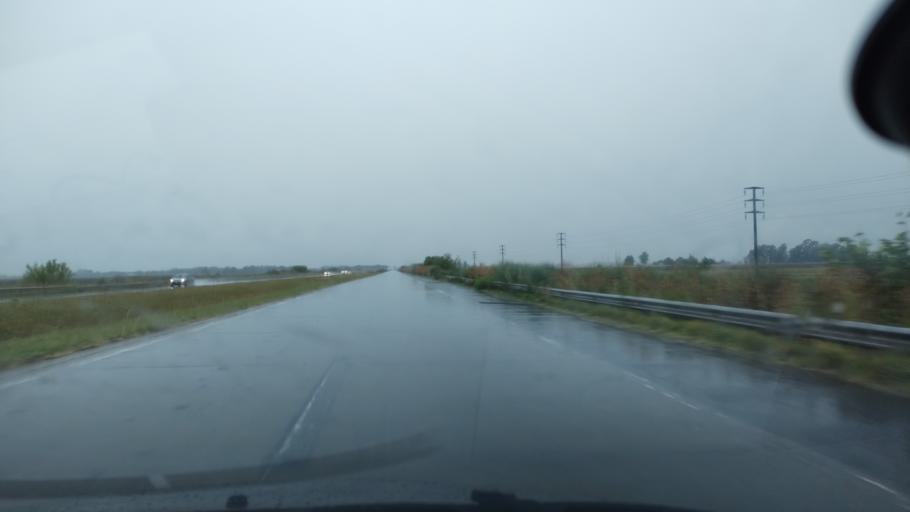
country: AR
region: Buenos Aires
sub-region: Partido de San Vicente
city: San Vicente
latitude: -35.0639
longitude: -58.4733
